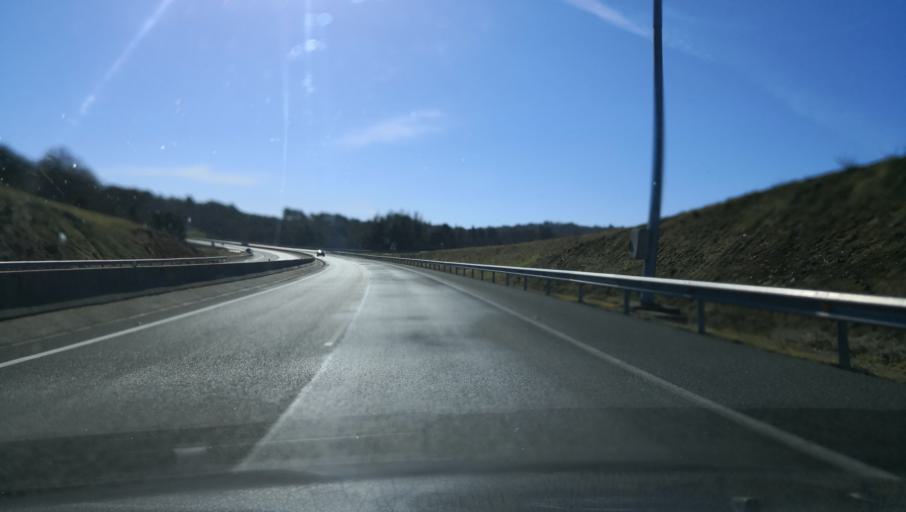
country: ES
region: Galicia
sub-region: Provincia de Pontevedra
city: Lalin
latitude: 42.6379
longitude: -8.1319
